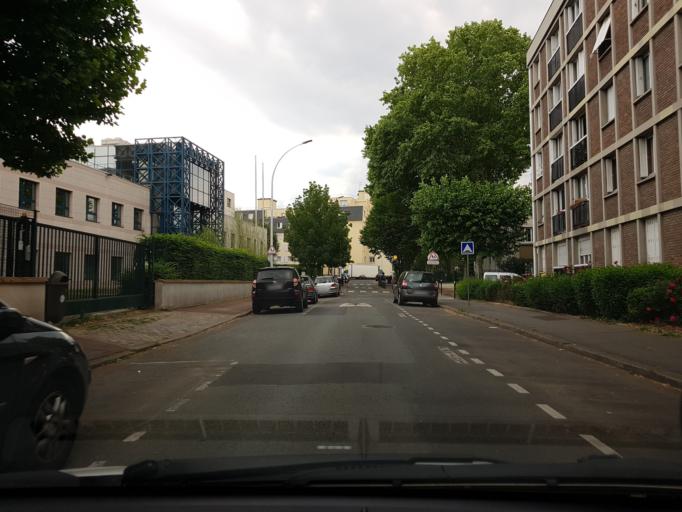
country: FR
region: Ile-de-France
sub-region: Departement du Val-de-Marne
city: Gentilly
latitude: 48.8124
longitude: 2.3480
